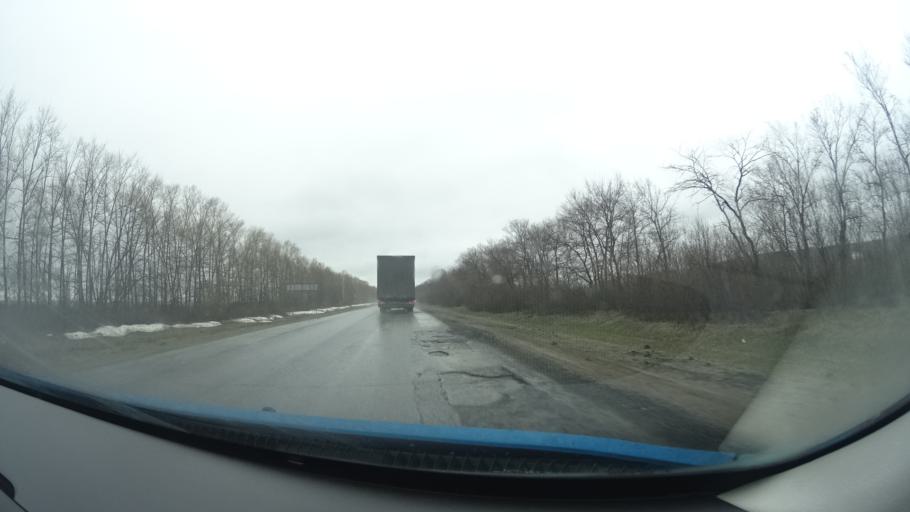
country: RU
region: Bashkortostan
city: Kandry
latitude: 54.5339
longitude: 54.1013
